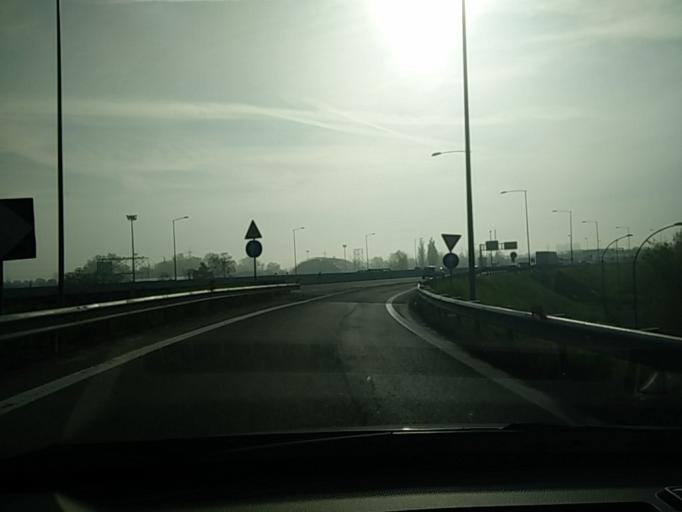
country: IT
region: Emilia-Romagna
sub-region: Provincia di Bologna
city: Bologna
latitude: 44.5216
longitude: 11.3656
